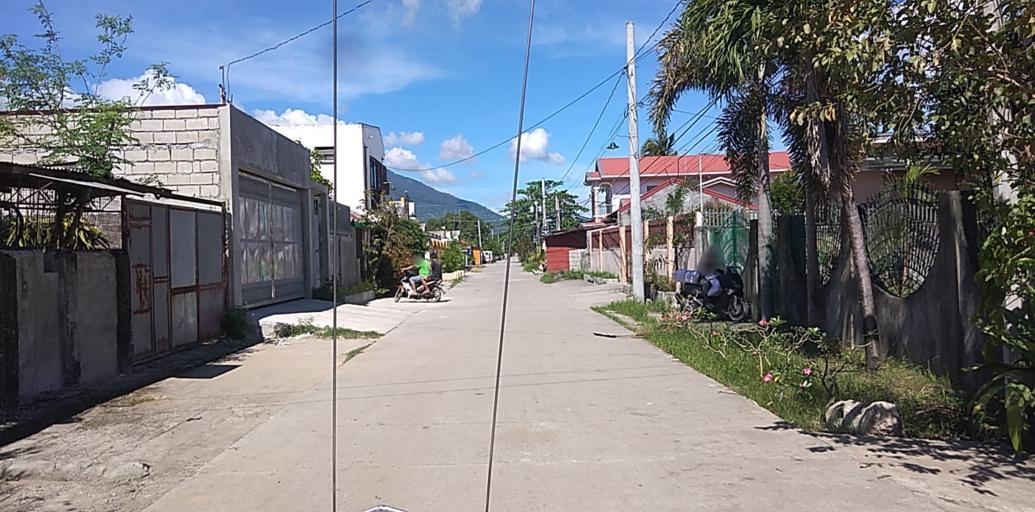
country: PH
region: Central Luzon
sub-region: Province of Pampanga
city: Arayat
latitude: 15.1349
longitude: 120.7752
